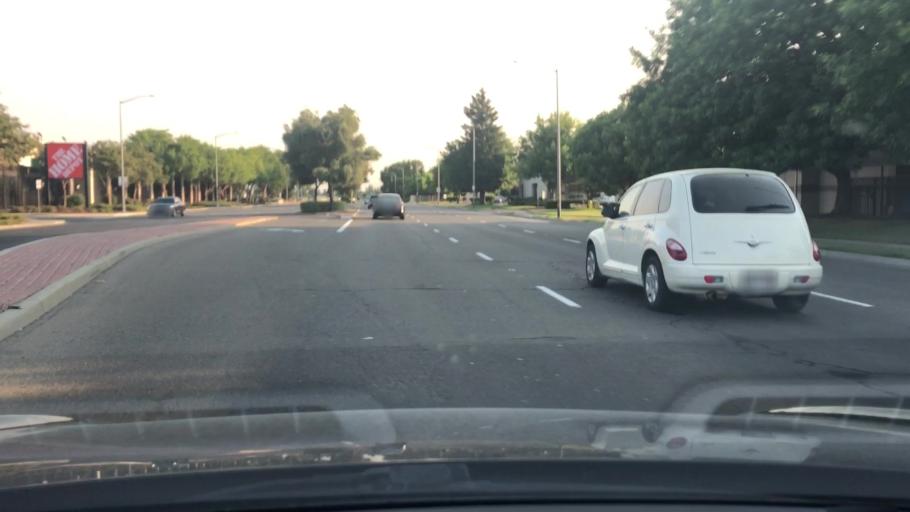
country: US
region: California
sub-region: Fresno County
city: Clovis
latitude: 36.8095
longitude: -119.7272
